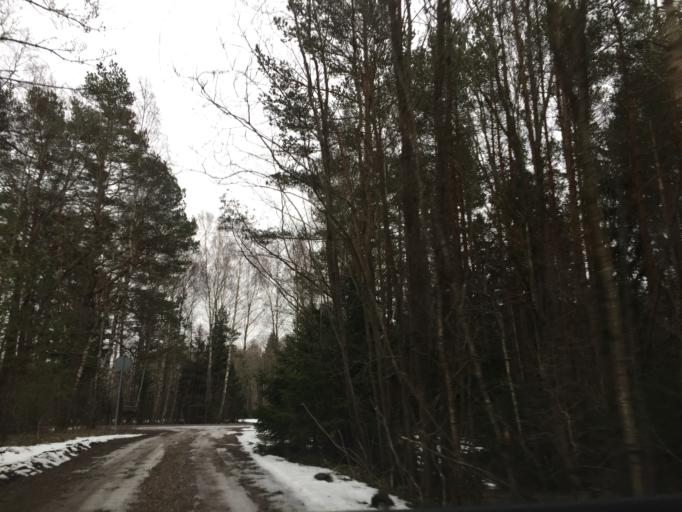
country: EE
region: Saare
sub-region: Kuressaare linn
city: Kuressaare
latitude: 58.4781
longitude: 22.2525
